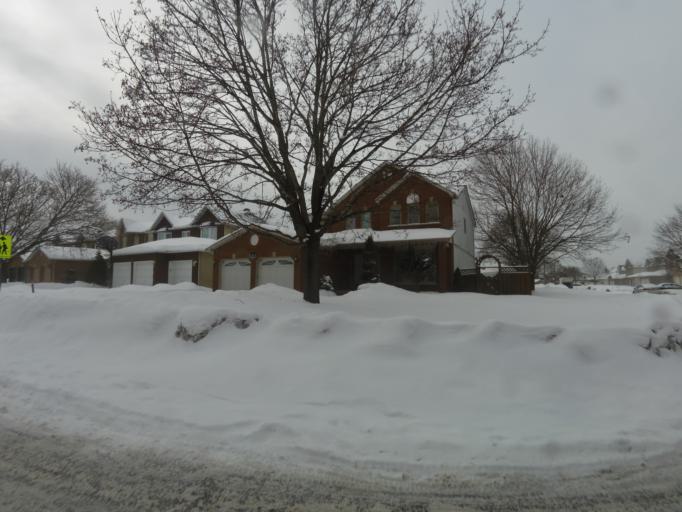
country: CA
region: Ontario
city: Ottawa
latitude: 45.3760
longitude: -75.6065
